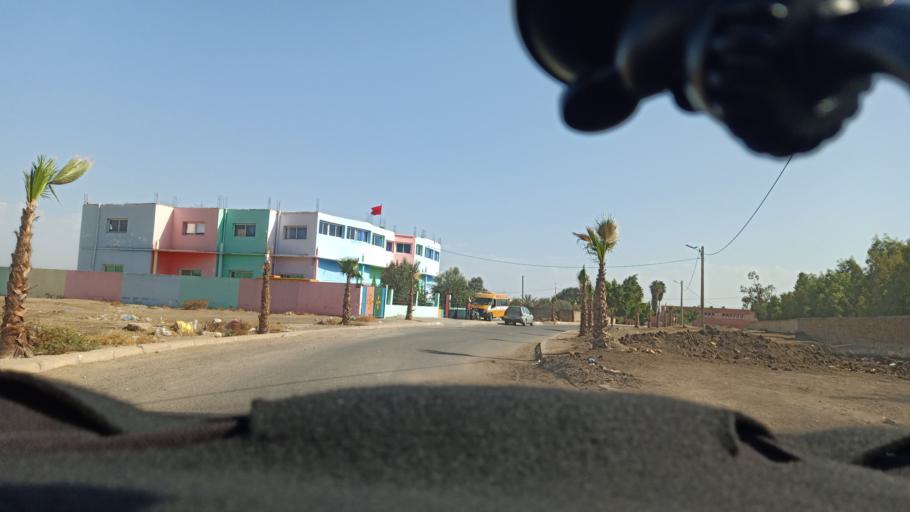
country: MA
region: Doukkala-Abda
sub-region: Safi
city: Youssoufia
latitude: 32.3490
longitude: -8.8346
